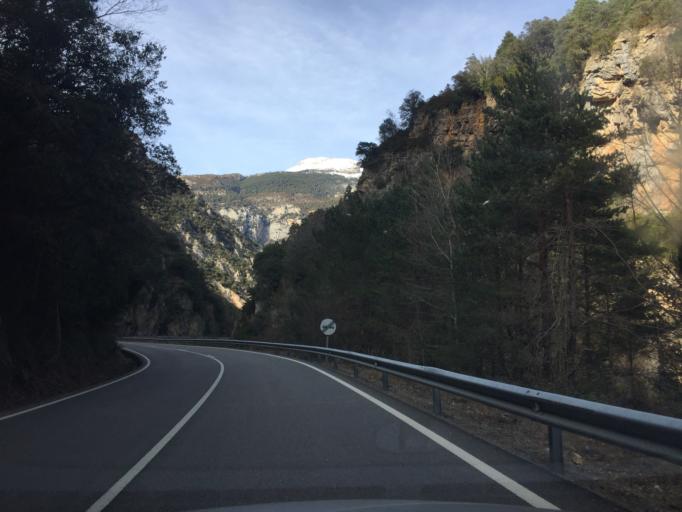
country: ES
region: Aragon
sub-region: Provincia de Huesca
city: Bielsa
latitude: 42.5688
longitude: 0.2058
